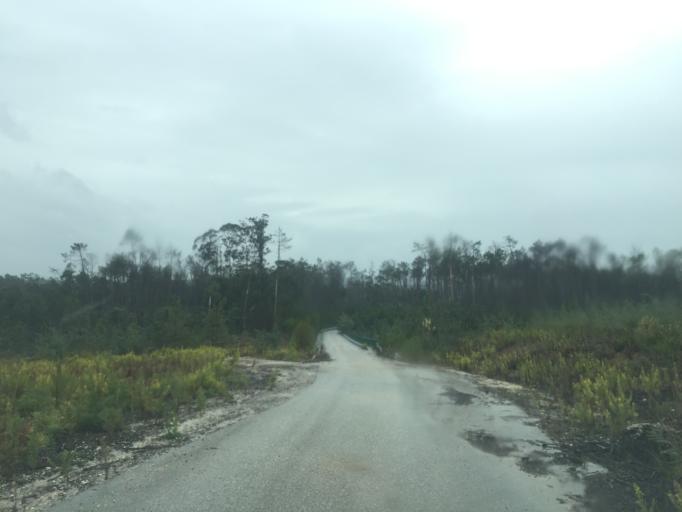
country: PT
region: Coimbra
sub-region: Figueira da Foz
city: Lavos
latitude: 40.0719
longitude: -8.7849
